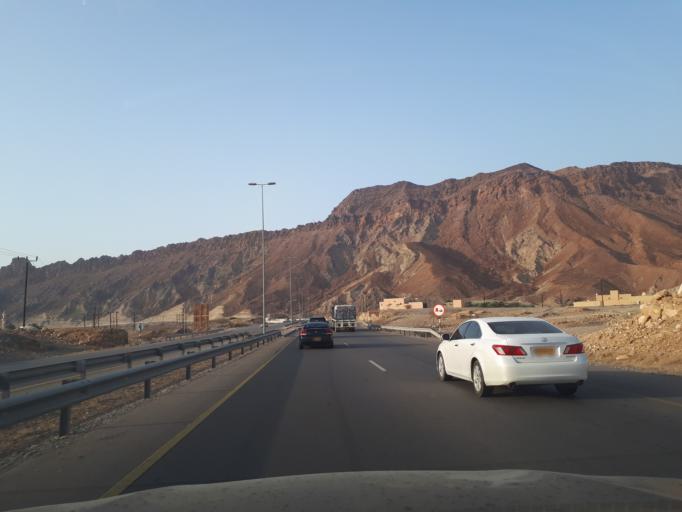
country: OM
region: Muhafazat ad Dakhiliyah
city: Bidbid
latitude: 23.4417
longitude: 58.1210
